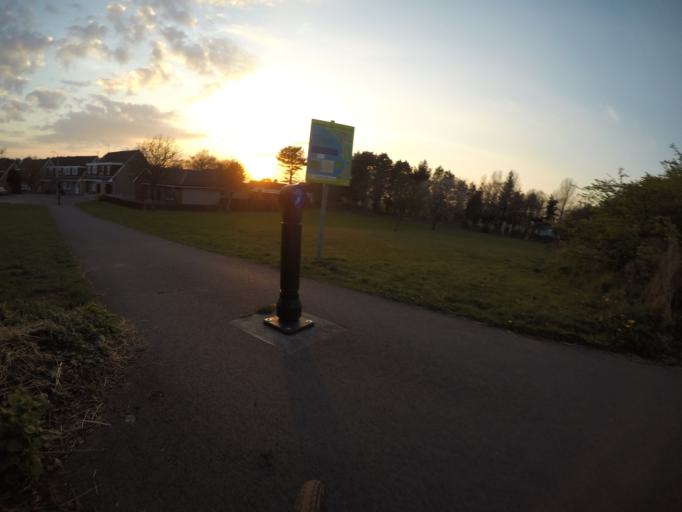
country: GB
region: Scotland
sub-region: South Ayrshire
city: Troon
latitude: 55.5680
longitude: -4.6392
